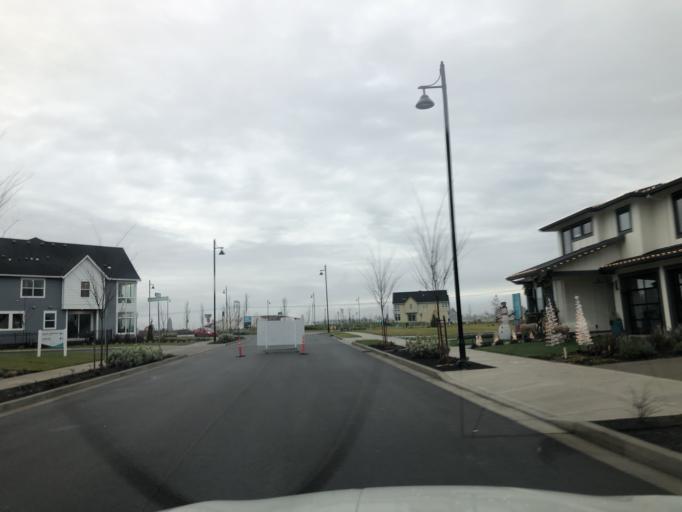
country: US
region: Oregon
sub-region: Washington County
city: Aloha
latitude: 45.4932
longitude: -122.9058
